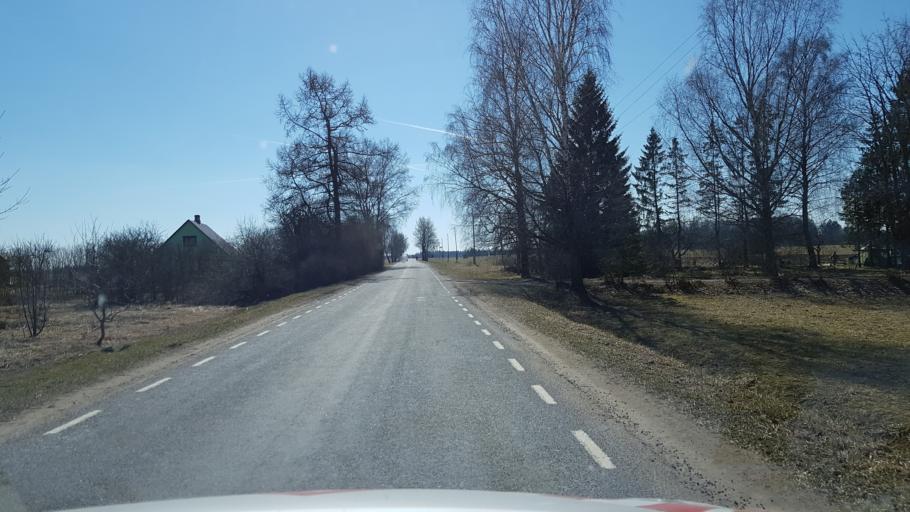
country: EE
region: Laeaene-Virumaa
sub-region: Vaeike-Maarja vald
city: Vaike-Maarja
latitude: 59.0975
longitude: 26.1967
